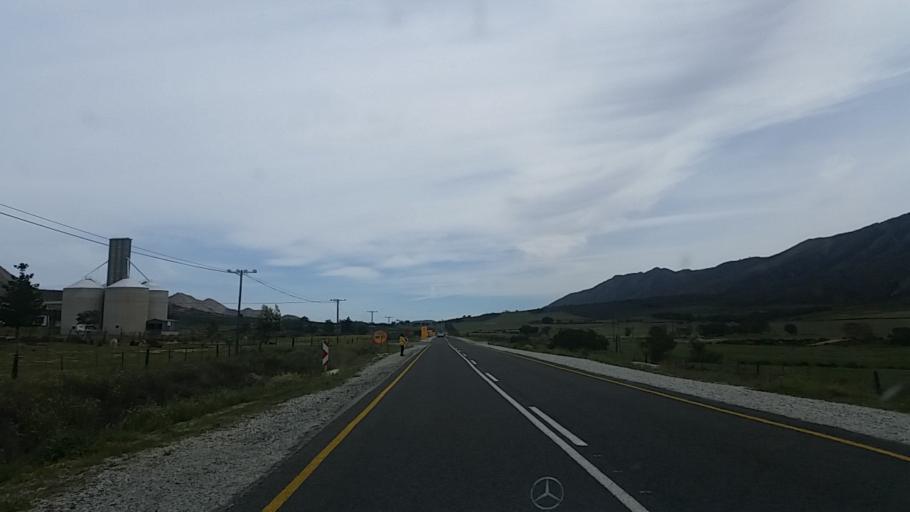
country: ZA
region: Western Cape
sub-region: Eden District Municipality
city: George
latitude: -33.8310
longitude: 22.4306
